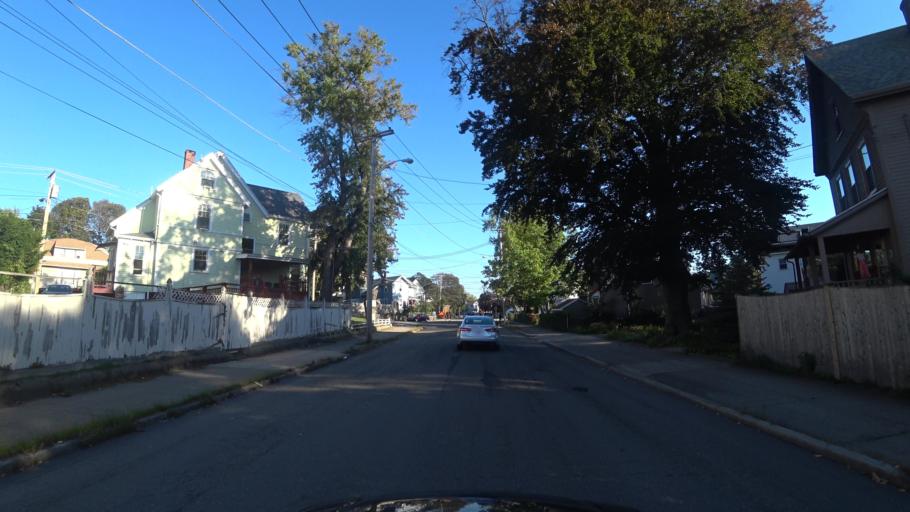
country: US
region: Massachusetts
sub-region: Middlesex County
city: Malden
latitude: 42.4175
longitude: -71.0700
